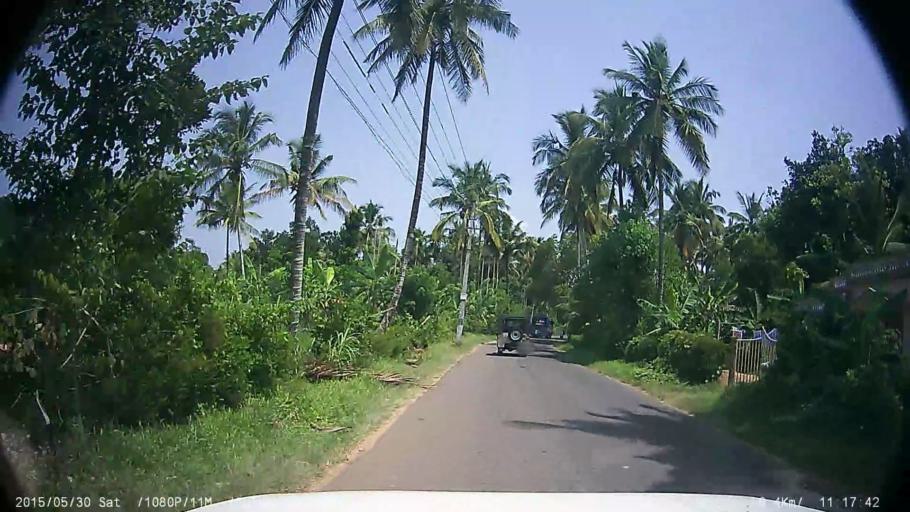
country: IN
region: Kerala
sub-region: Wayanad
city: Panamaram
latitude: 11.7808
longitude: 76.0485
